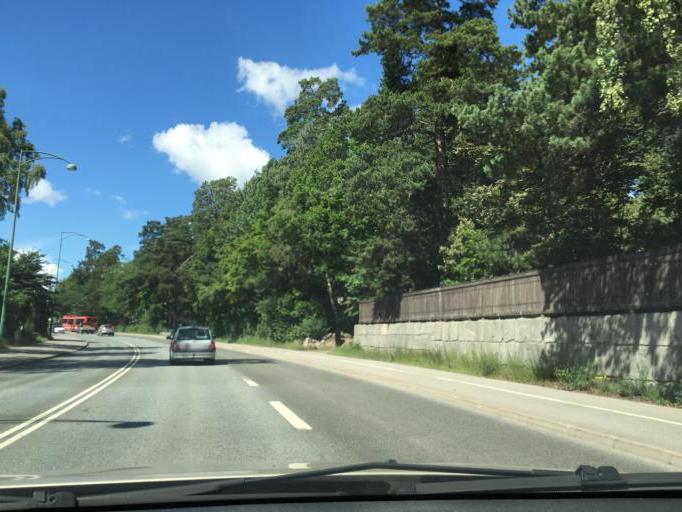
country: SE
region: Stockholm
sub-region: Nacka Kommun
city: Nacka
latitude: 59.3091
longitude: 18.1697
